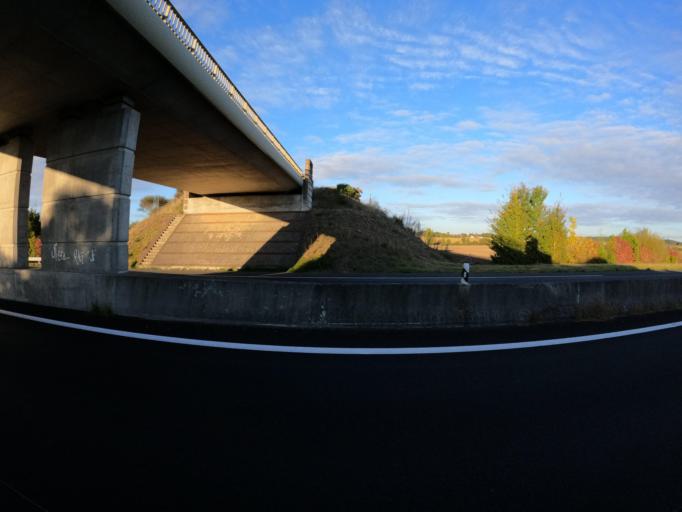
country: FR
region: Pays de la Loire
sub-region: Departement de Maine-et-Loire
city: Saint-Jean
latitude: 47.2824
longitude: -0.3506
